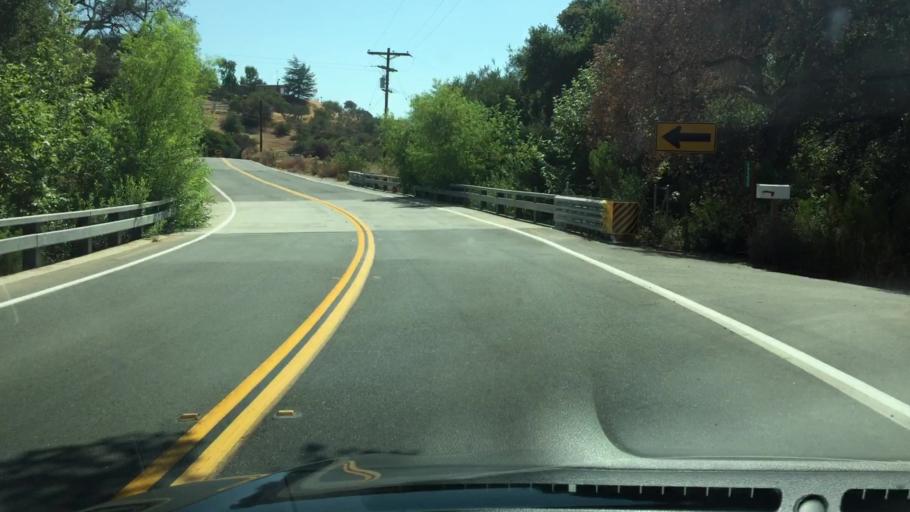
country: US
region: California
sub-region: San Diego County
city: Alpine
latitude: 32.7549
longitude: -116.7728
